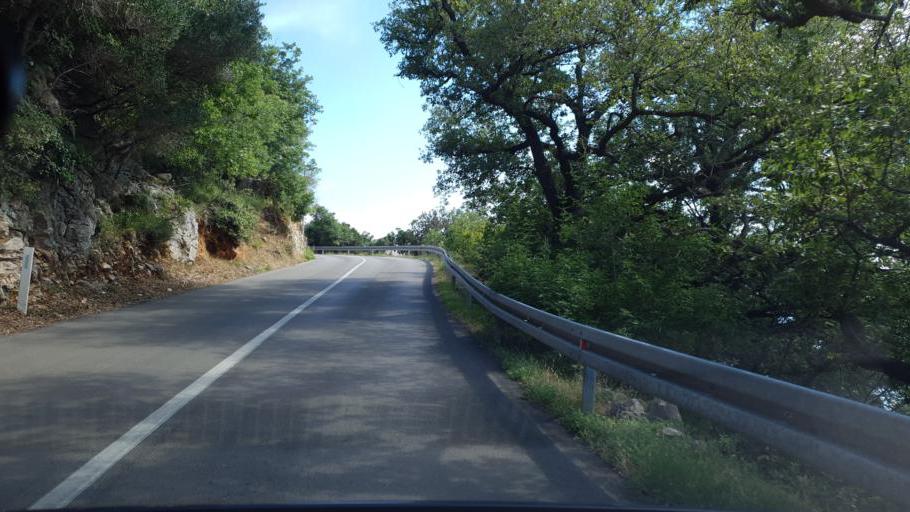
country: HR
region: Primorsko-Goranska
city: Punat
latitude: 44.9650
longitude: 14.6799
